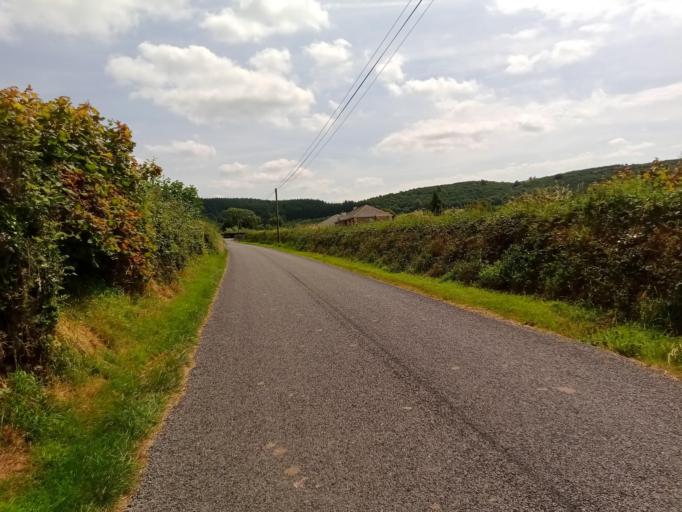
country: IE
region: Leinster
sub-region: Laois
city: Rathdowney
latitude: 52.8092
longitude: -7.4684
